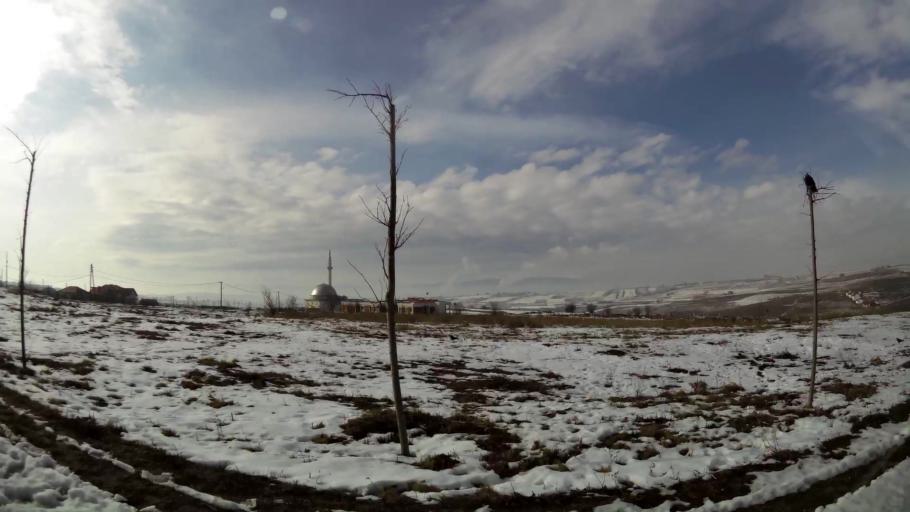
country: XK
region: Pristina
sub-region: Komuna e Prishtines
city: Pristina
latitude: 42.6748
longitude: 21.1513
